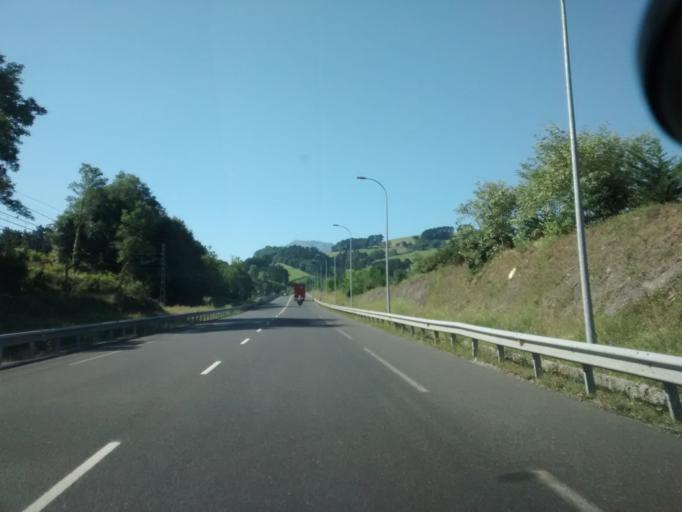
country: ES
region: Basque Country
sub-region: Provincia de Guipuzcoa
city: Zumaia
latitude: 43.2888
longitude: -2.2546
